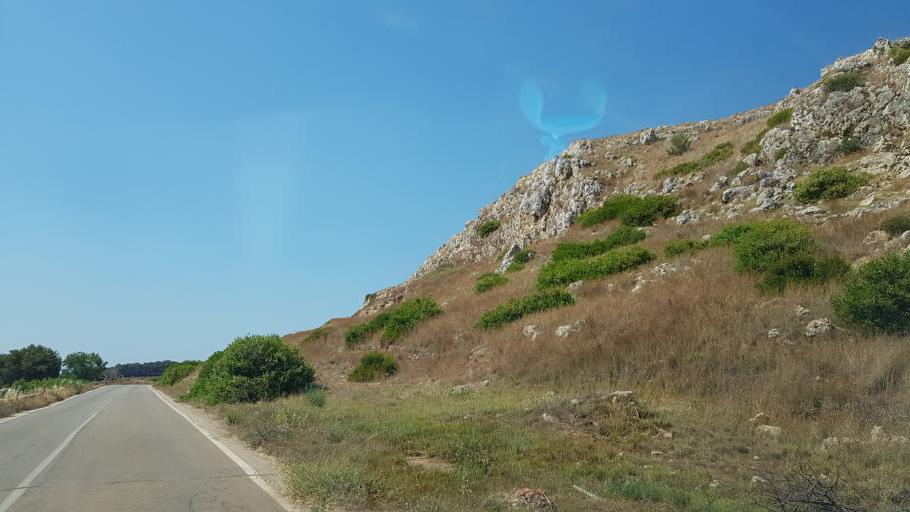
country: IT
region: Apulia
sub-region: Provincia di Lecce
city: Nardo
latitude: 40.1699
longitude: 17.9488
